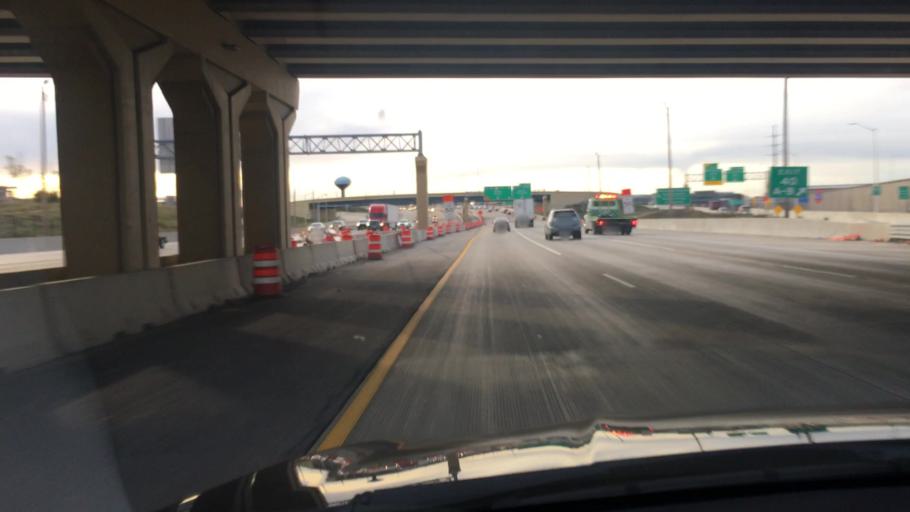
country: US
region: Wisconsin
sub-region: Milwaukee County
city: Wauwatosa
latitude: 43.0505
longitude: -88.0403
